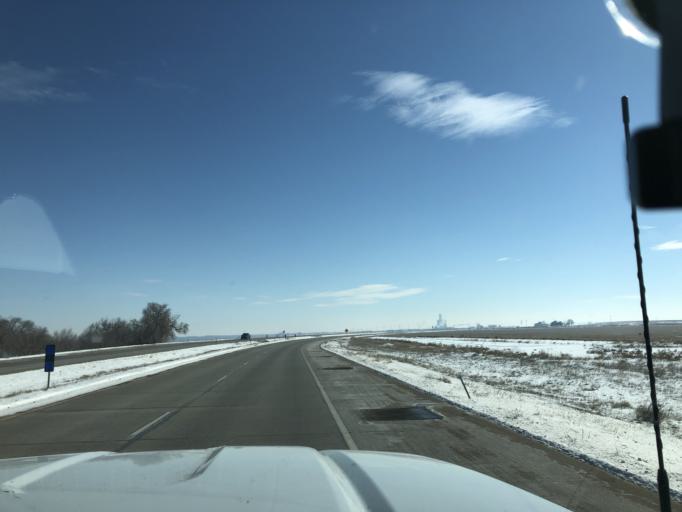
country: US
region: Colorado
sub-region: Weld County
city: Kersey
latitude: 40.3872
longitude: -104.5379
